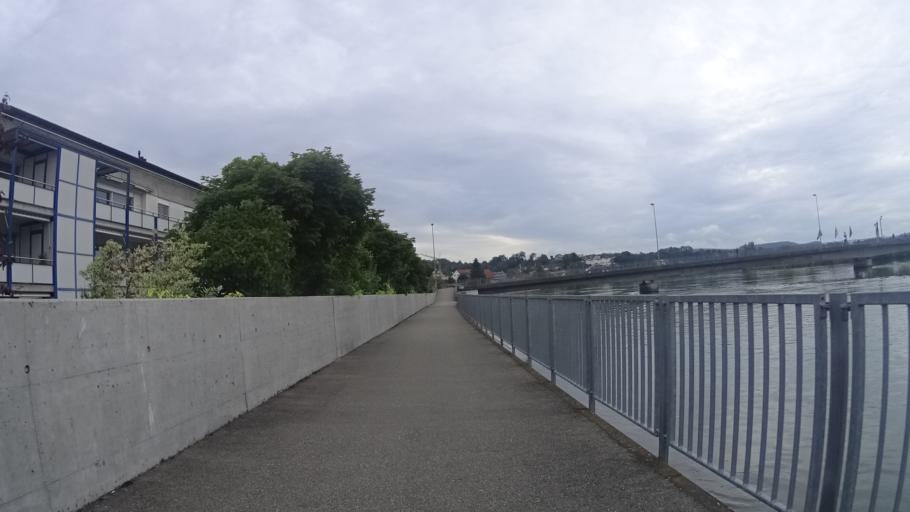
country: CH
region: Aargau
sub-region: Bezirk Zurzach
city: Klingnau
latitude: 47.5745
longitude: 8.2525
